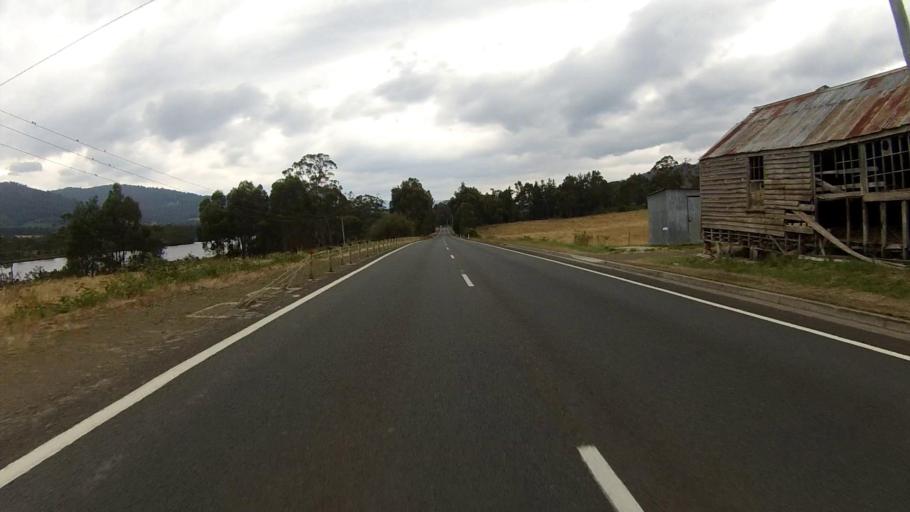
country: AU
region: Tasmania
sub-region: Huon Valley
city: Franklin
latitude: -43.0830
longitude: 147.0307
